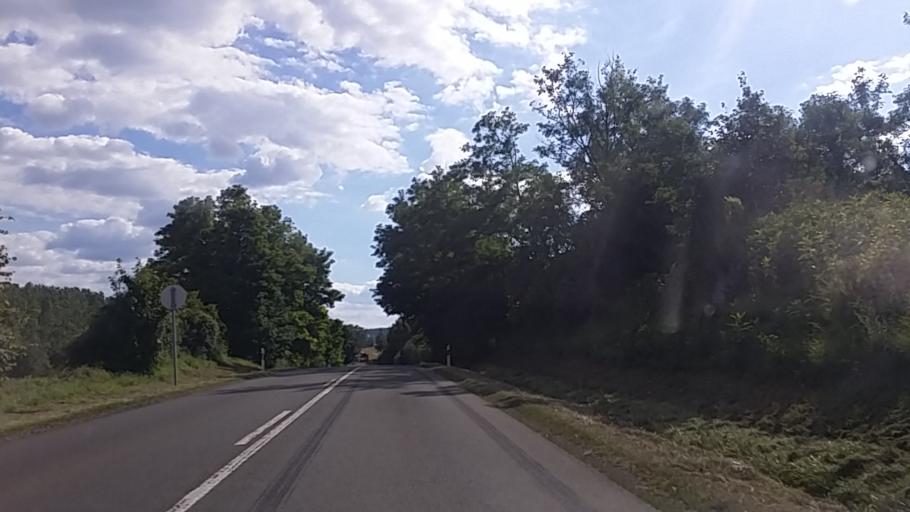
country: HU
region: Baranya
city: Sasd
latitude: 46.2813
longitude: 18.1103
